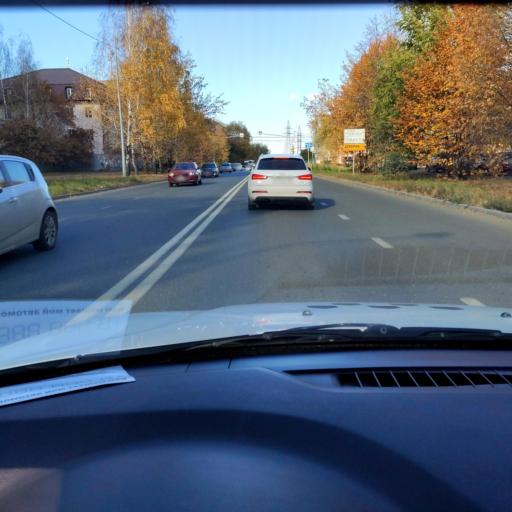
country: RU
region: Samara
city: Tol'yatti
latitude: 53.5387
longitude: 49.4096
